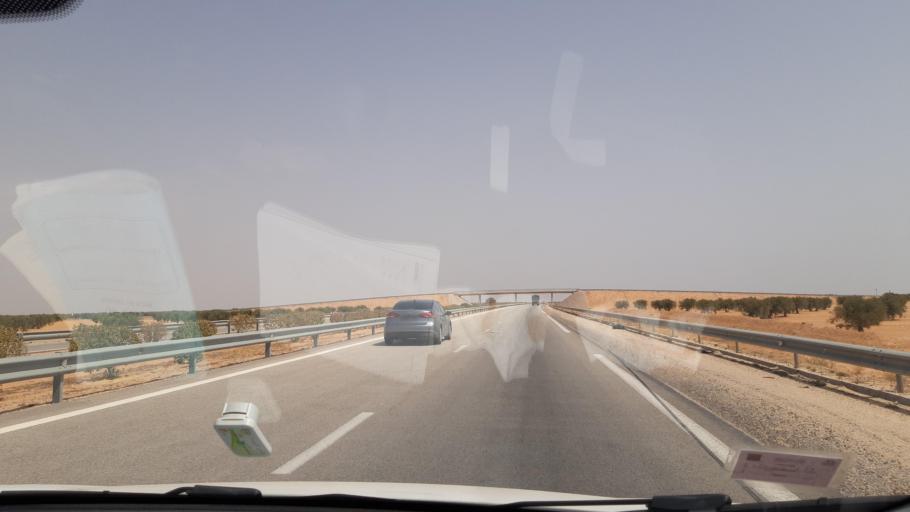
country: TN
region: Safaqis
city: Bi'r `Ali Bin Khalifah
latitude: 34.5287
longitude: 10.1179
